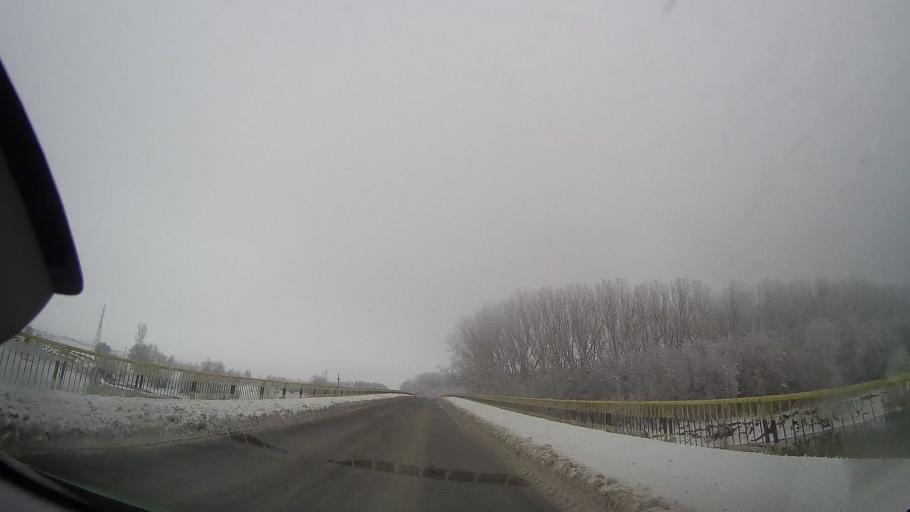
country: RO
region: Neamt
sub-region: Comuna Horia
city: Cotu Vames
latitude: 46.8823
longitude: 26.9711
